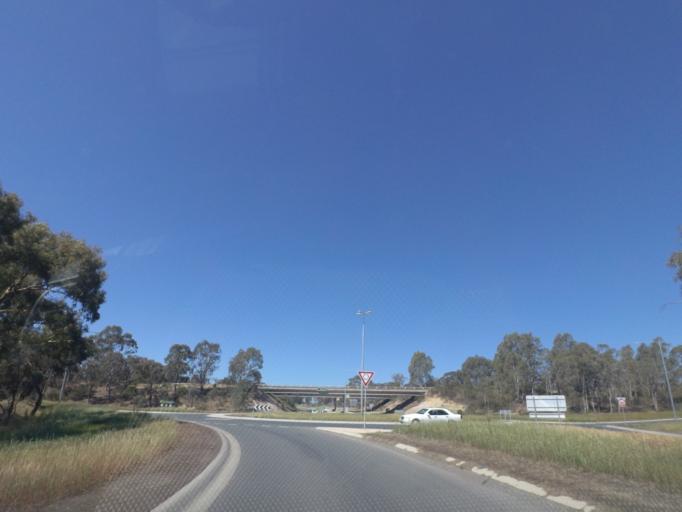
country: AU
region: Victoria
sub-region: Murrindindi
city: Kinglake West
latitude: -37.0309
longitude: 145.0998
